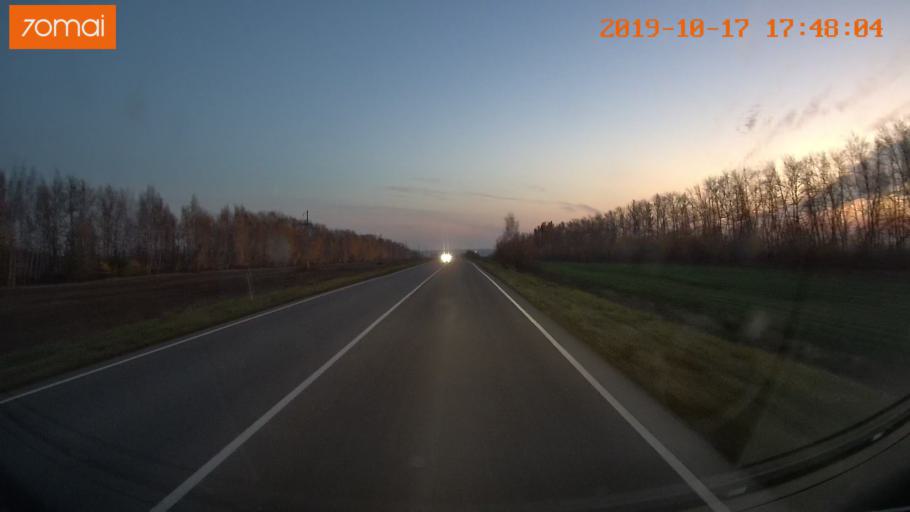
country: RU
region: Tula
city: Yepifan'
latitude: 53.6980
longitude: 38.6967
